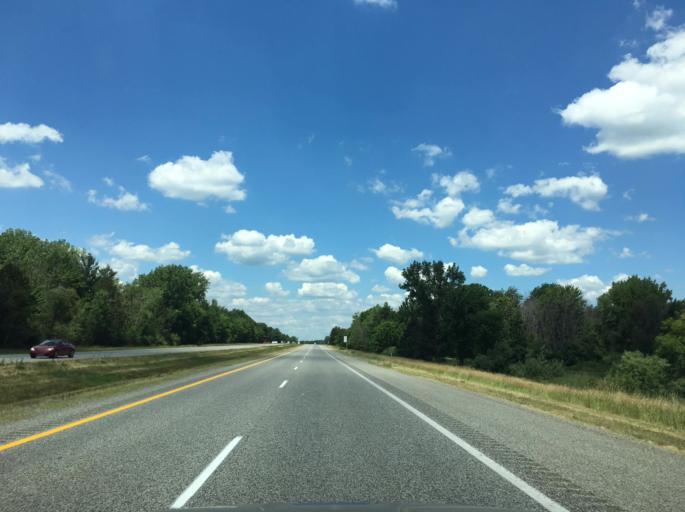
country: US
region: Michigan
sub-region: Midland County
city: Midland
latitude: 43.6470
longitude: -84.1935
